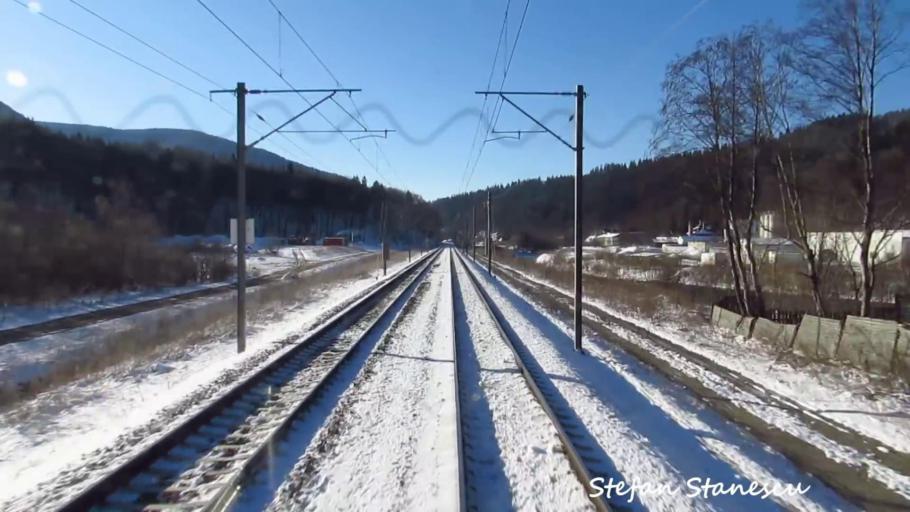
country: RO
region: Prahova
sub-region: Oras Busteni
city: Poiana Tapului
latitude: 45.3757
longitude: 25.5425
